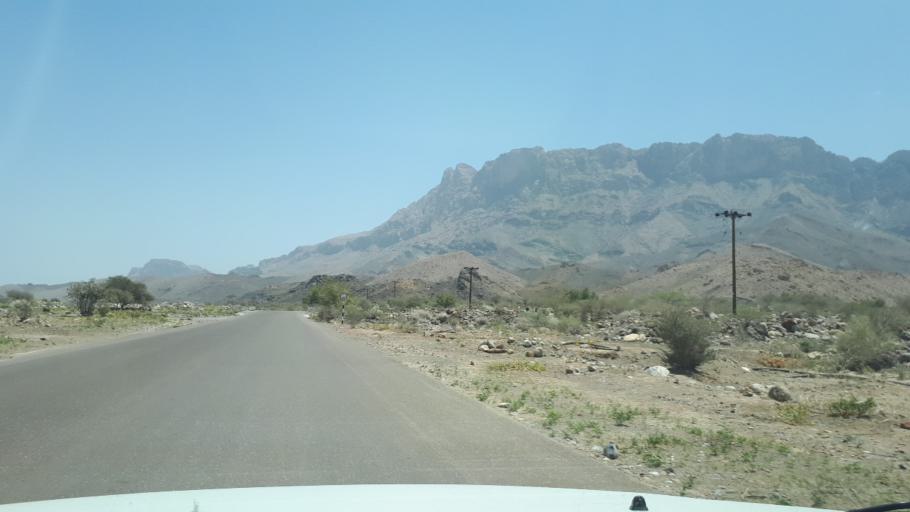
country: OM
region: Muhafazat ad Dakhiliyah
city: Bahla'
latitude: 23.1664
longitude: 57.1595
